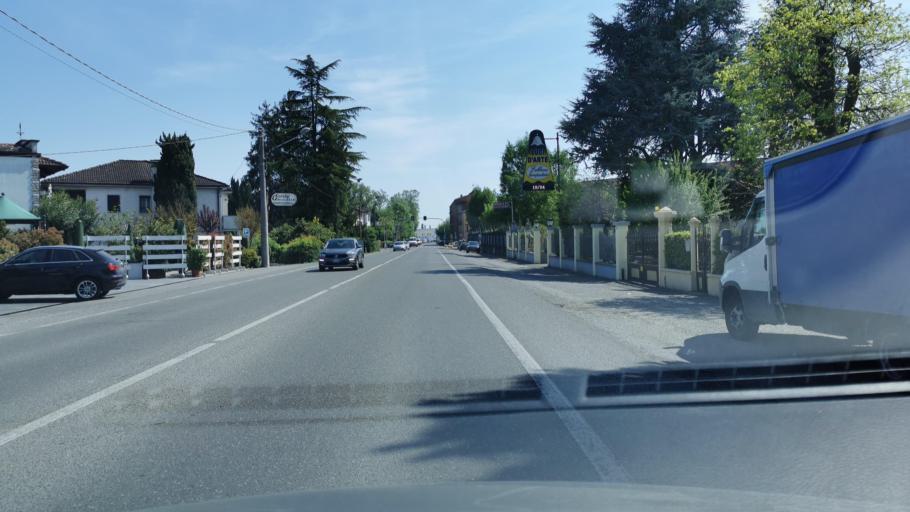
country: IT
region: Emilia-Romagna
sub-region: Provincia di Piacenza
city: Castelvetro Piacentino
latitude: 45.1158
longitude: 9.9926
